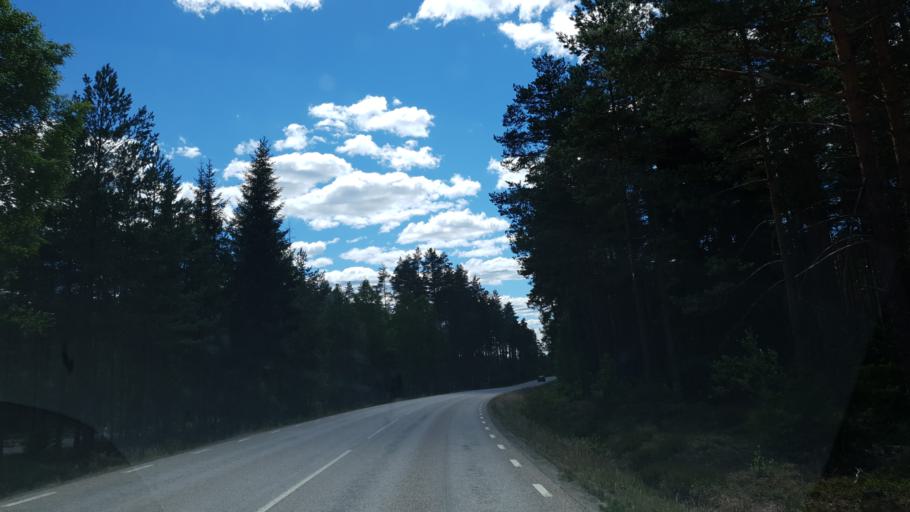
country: SE
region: Kronoberg
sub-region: Lessebo Kommun
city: Lessebo
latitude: 56.8141
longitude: 15.3742
